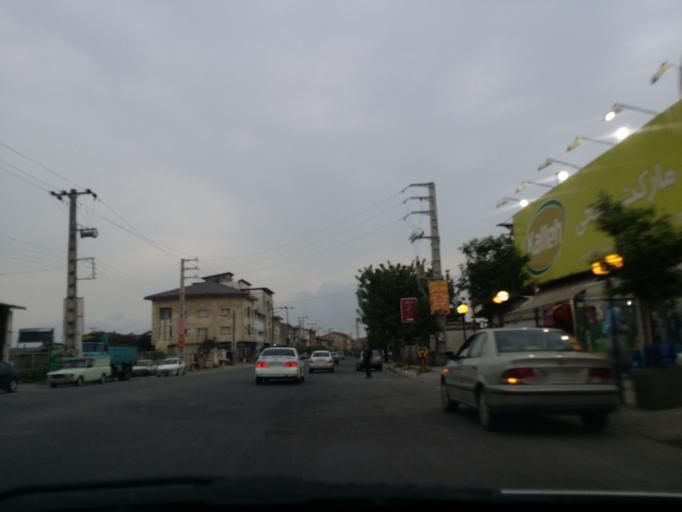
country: IR
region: Mazandaran
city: `Abbasabad
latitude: 36.7218
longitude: 51.1032
